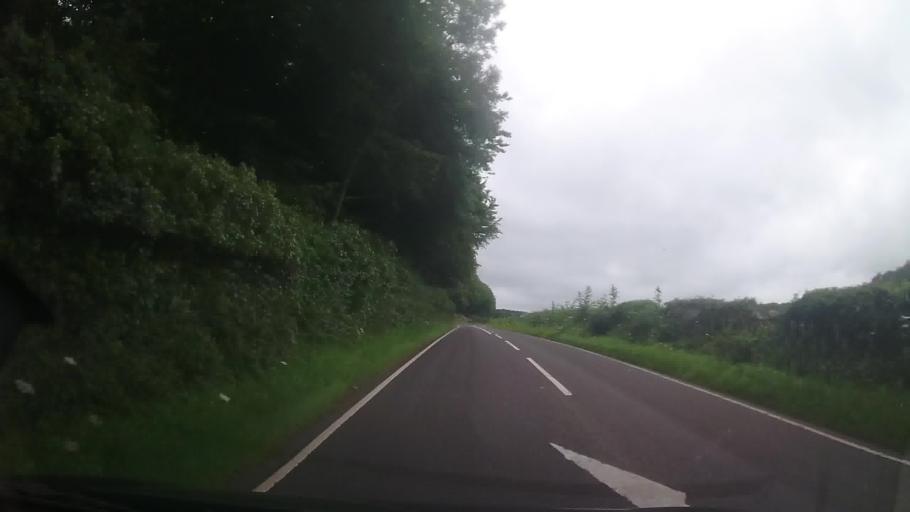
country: GB
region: Wales
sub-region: Anglesey
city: Llanfairpwllgwyngyll
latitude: 53.2103
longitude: -4.2162
